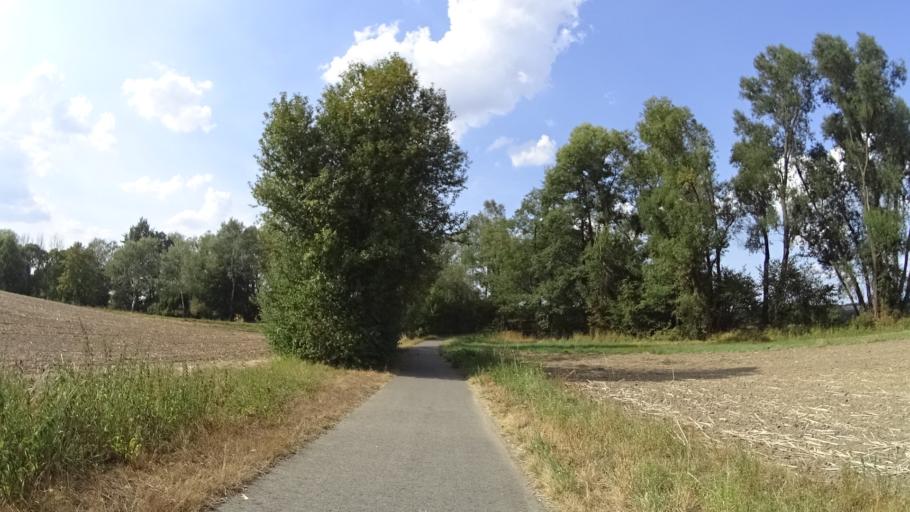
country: DE
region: Saxony
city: Ostritz
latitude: 51.0293
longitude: 14.9368
